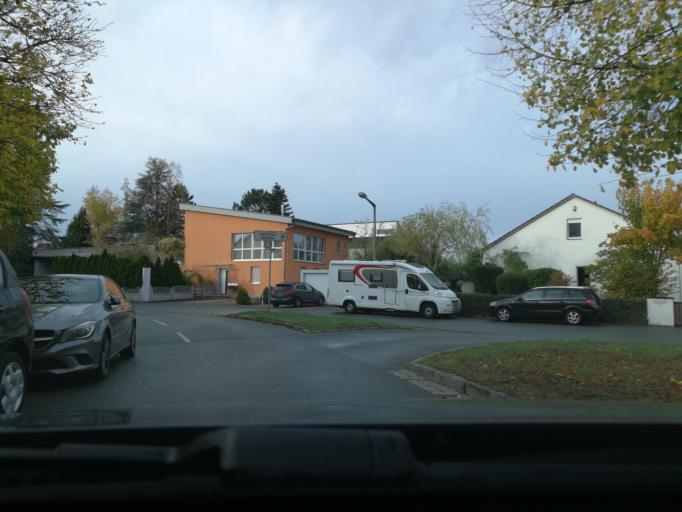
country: DE
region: Bavaria
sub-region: Regierungsbezirk Mittelfranken
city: Furth
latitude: 49.4820
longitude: 10.9511
